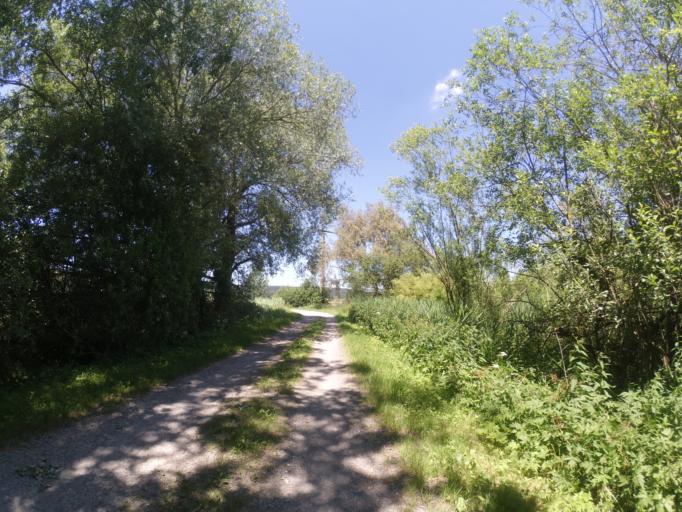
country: DE
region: Baden-Wuerttemberg
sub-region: Tuebingen Region
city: Bad Wurzach
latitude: 47.8986
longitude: 9.8486
